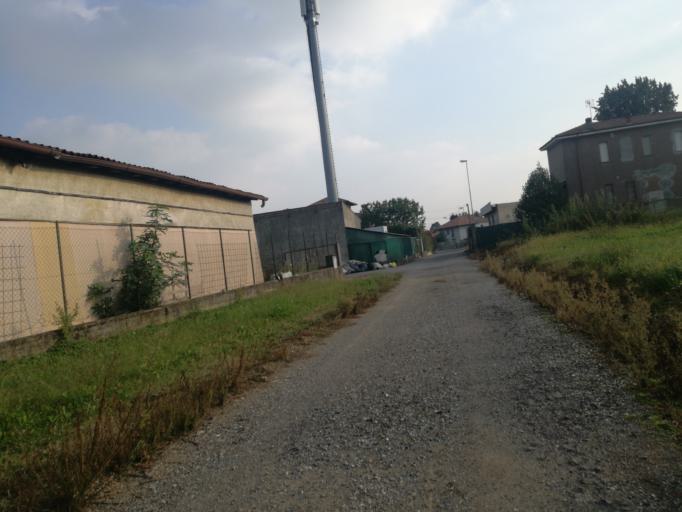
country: IT
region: Lombardy
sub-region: Provincia di Monza e Brianza
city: Porto d'Adda
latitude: 45.6543
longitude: 9.4631
